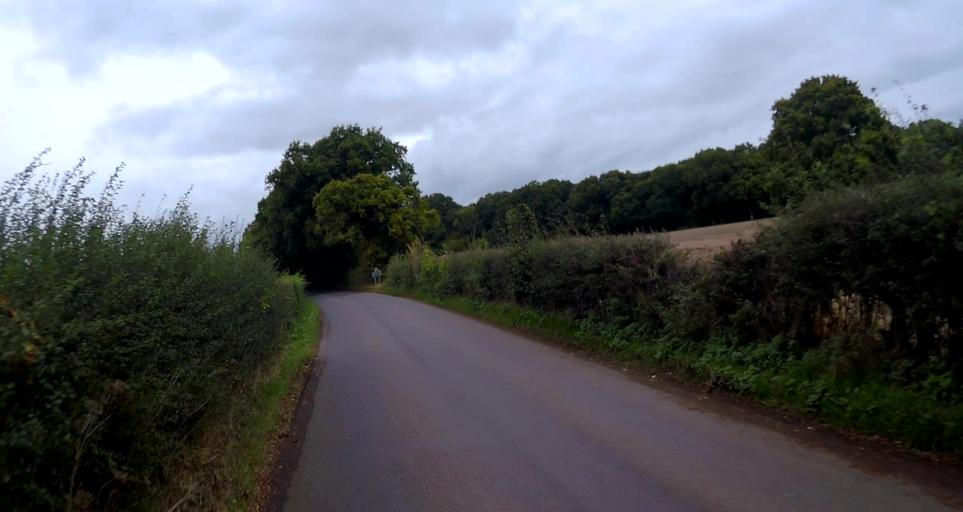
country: GB
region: England
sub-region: Hampshire
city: Four Marks
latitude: 51.1396
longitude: -1.0833
